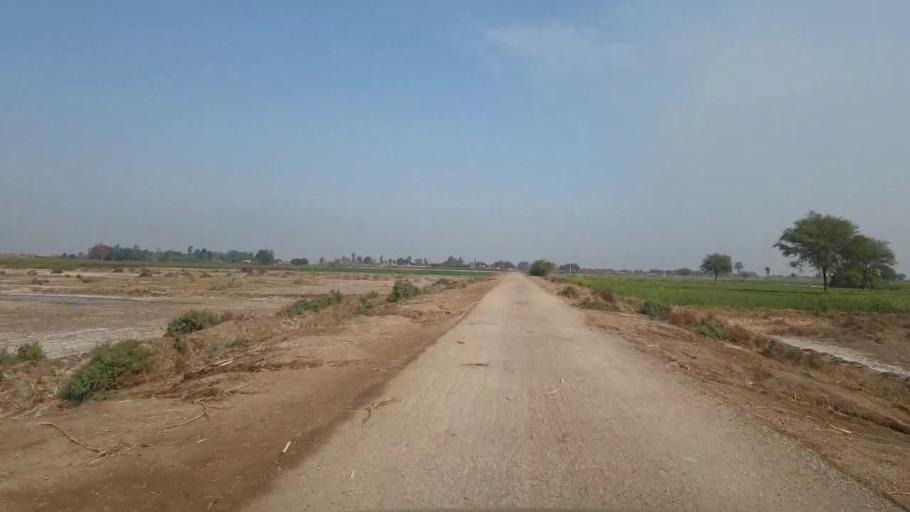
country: PK
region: Sindh
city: Mirwah Gorchani
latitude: 25.3722
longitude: 69.1609
